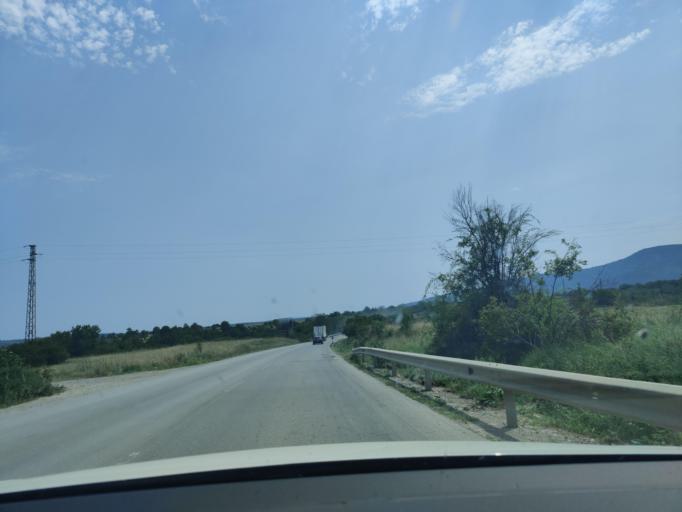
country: BG
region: Montana
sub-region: Obshtina Chiprovtsi
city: Chiprovtsi
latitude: 43.5038
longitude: 22.9925
